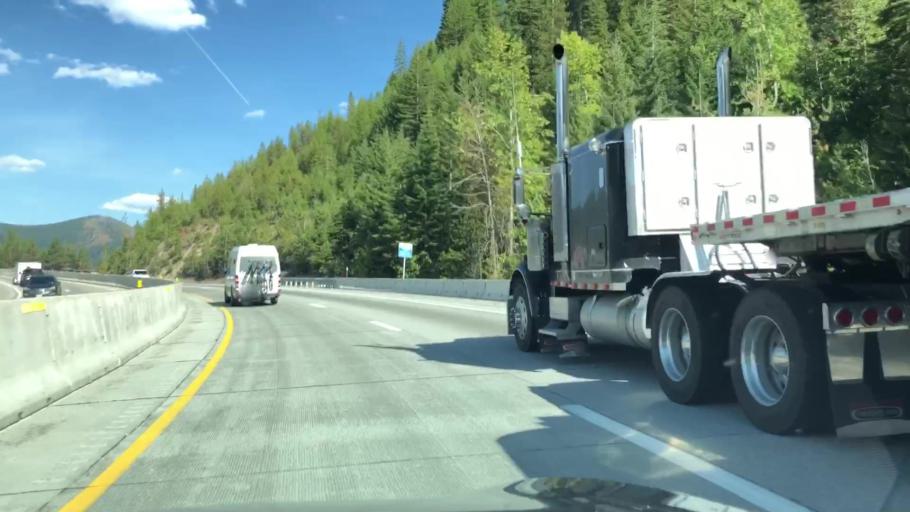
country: US
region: Idaho
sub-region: Shoshone County
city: Wallace
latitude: 47.4594
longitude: -115.7259
